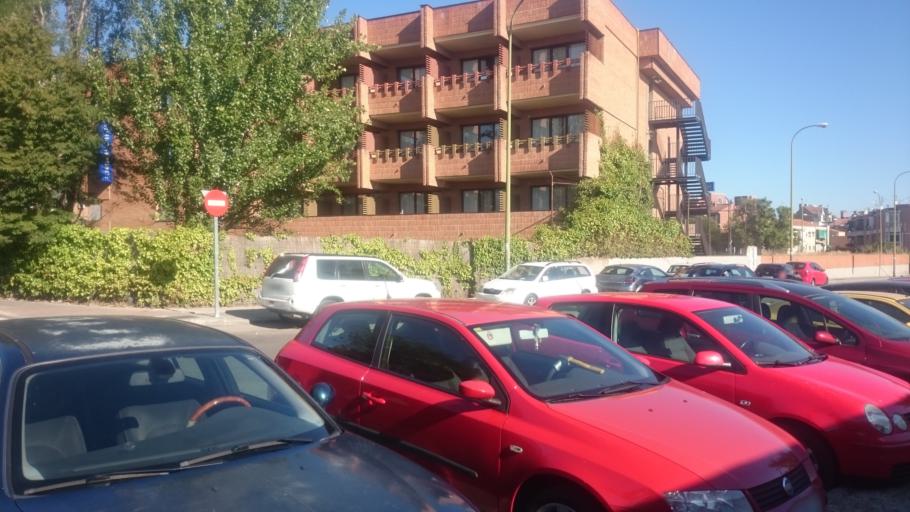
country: ES
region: Madrid
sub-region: Provincia de Madrid
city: Barajas de Madrid
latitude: 40.4686
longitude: -3.5799
